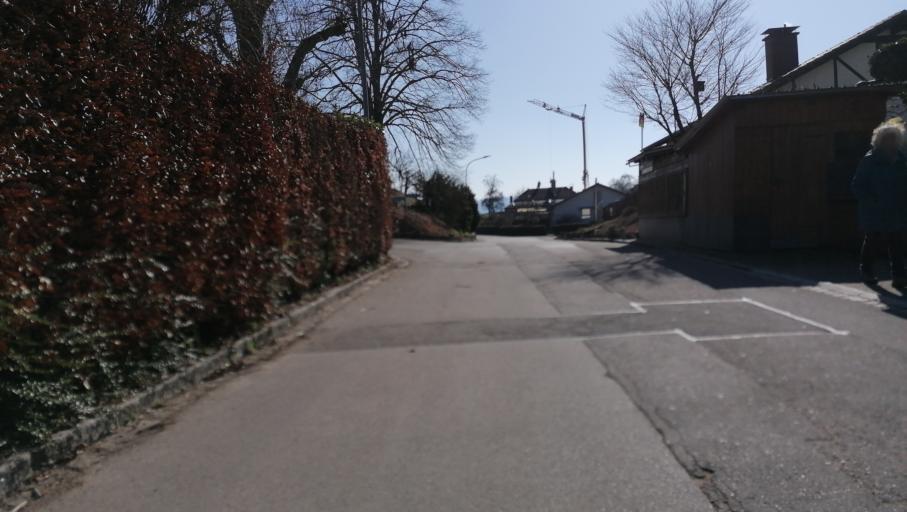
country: DE
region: Baden-Wuerttemberg
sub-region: Freiburg Region
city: Schworstadt
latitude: 47.5898
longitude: 7.9170
